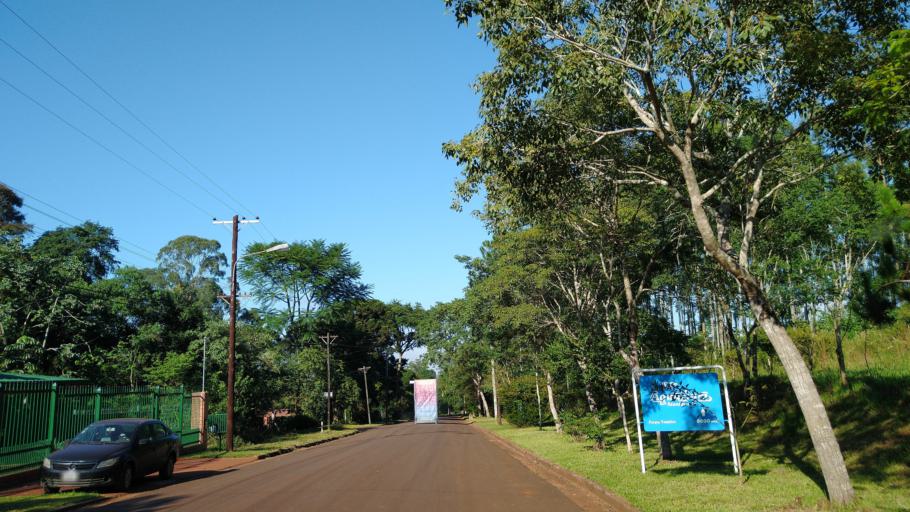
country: AR
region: Misiones
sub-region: Departamento de Montecarlo
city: Montecarlo
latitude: -26.5575
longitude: -54.7752
